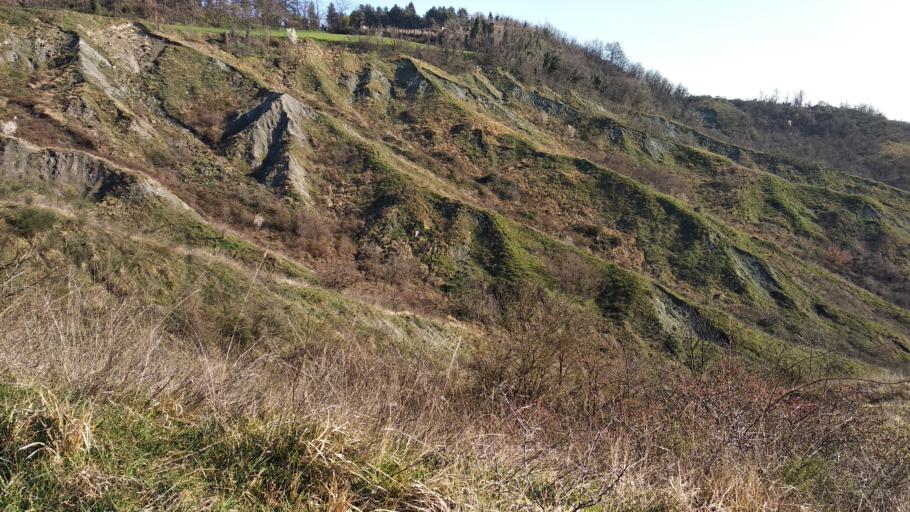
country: IT
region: Emilia-Romagna
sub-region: Provincia di Bologna
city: Pizzano
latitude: 44.3895
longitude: 11.4527
